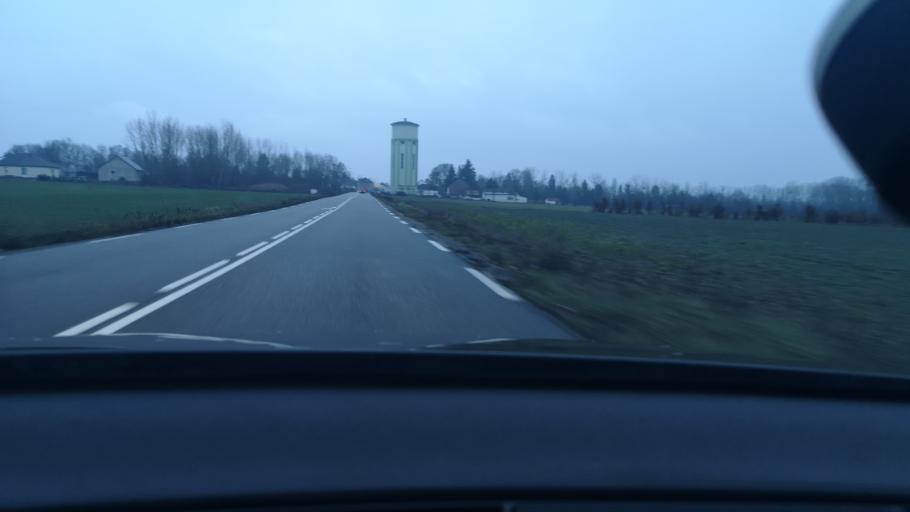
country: FR
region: Bourgogne
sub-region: Departement de la Cote-d'Or
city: Seurre
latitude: 47.0697
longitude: 5.0994
